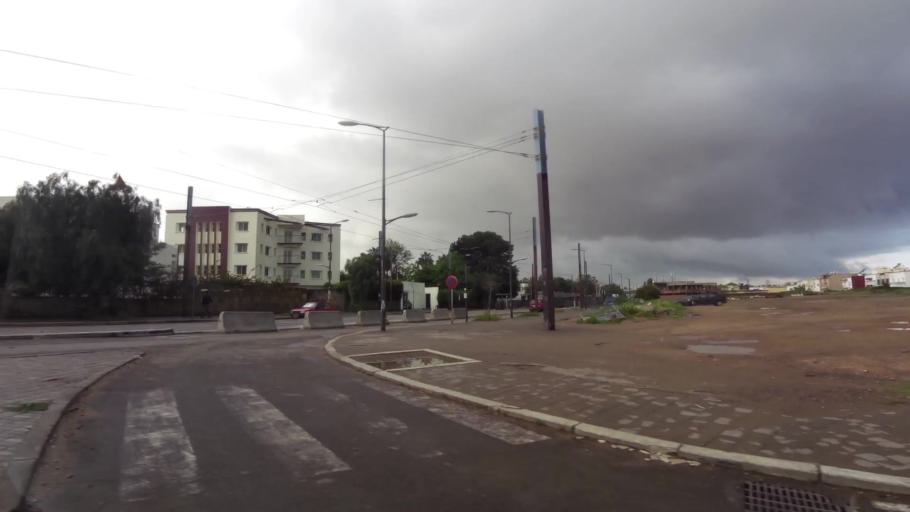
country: MA
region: Grand Casablanca
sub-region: Casablanca
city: Casablanca
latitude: 33.5463
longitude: -7.6562
